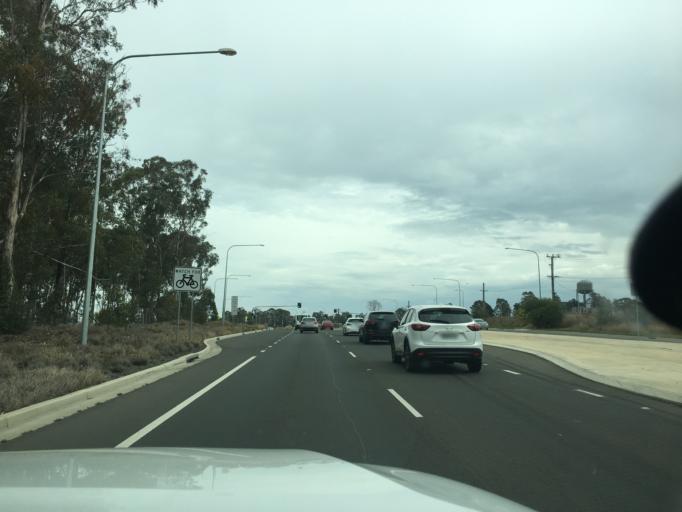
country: AU
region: New South Wales
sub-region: Campbelltown Municipality
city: Denham Court
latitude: -33.9812
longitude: 150.8011
